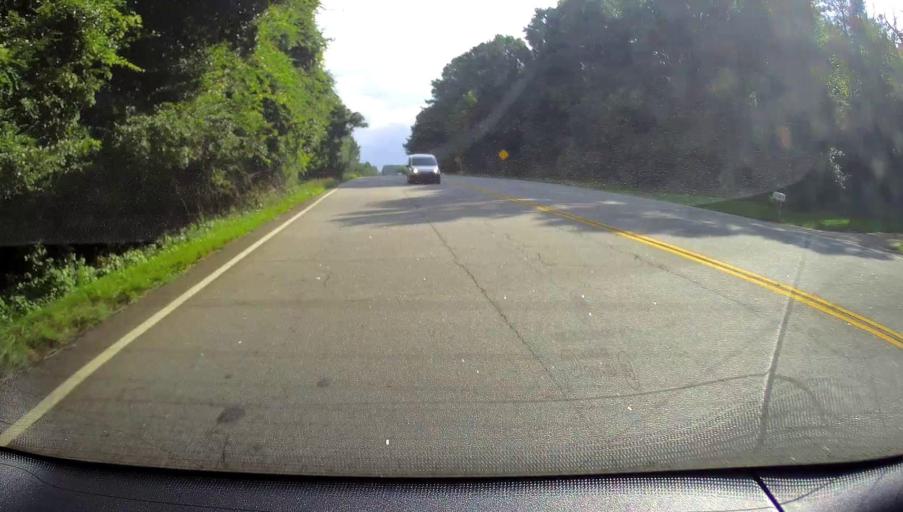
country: US
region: Georgia
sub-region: Coweta County
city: Senoia
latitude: 33.3121
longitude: -84.5282
